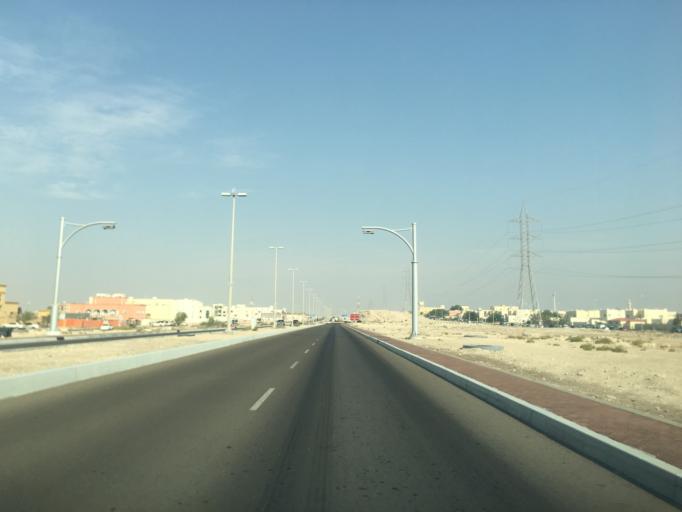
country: AE
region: Abu Dhabi
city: Abu Dhabi
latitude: 24.3023
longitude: 54.6537
